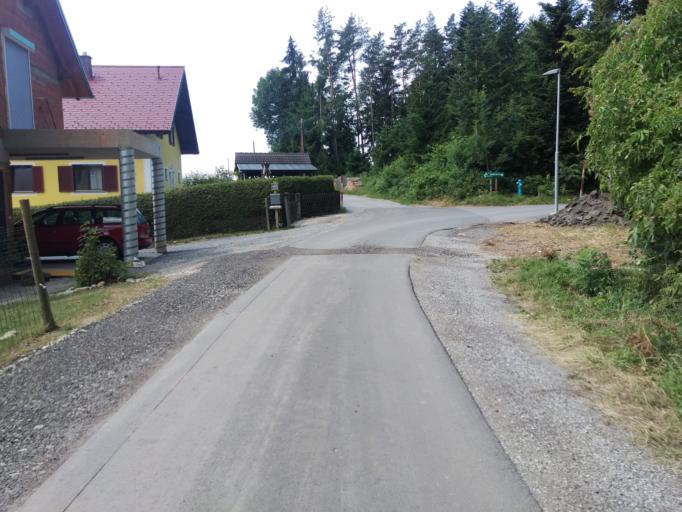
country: AT
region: Styria
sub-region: Graz Stadt
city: Mariatrost
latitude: 47.1276
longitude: 15.5076
